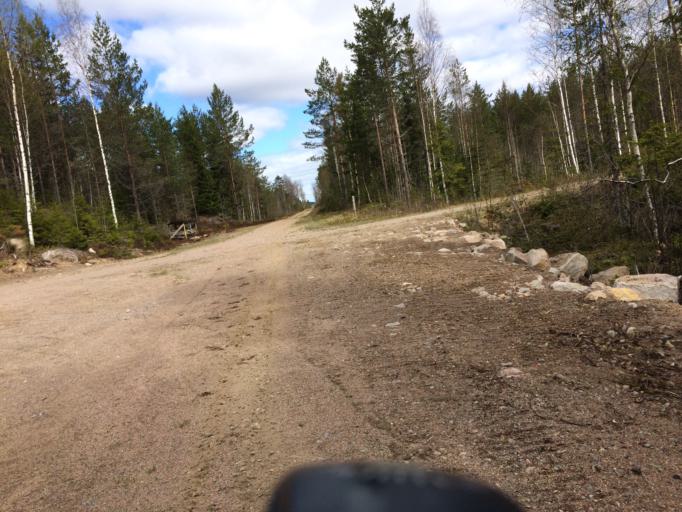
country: SE
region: OErebro
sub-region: Hallefors Kommun
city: Haellefors
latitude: 60.0560
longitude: 14.5225
